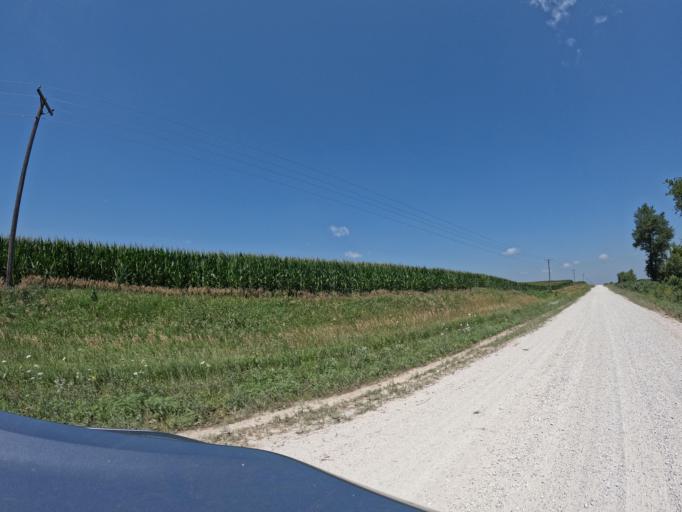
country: US
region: Iowa
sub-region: Keokuk County
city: Sigourney
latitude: 41.2717
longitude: -92.2381
